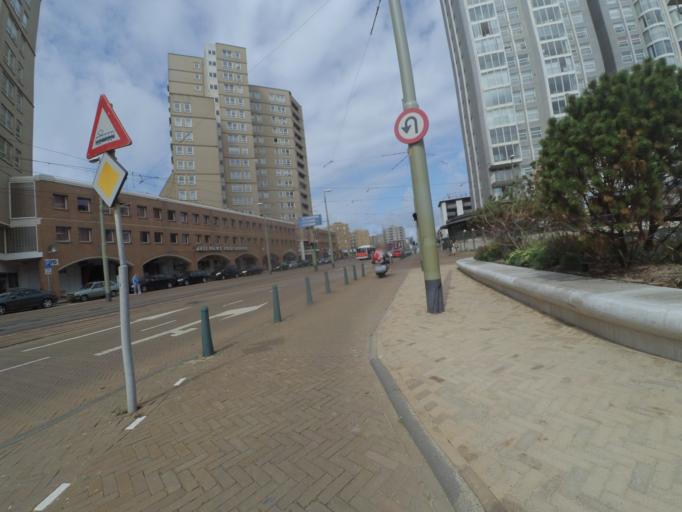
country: NL
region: South Holland
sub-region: Gemeente Den Haag
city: Scheveningen
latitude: 52.1139
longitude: 4.2843
